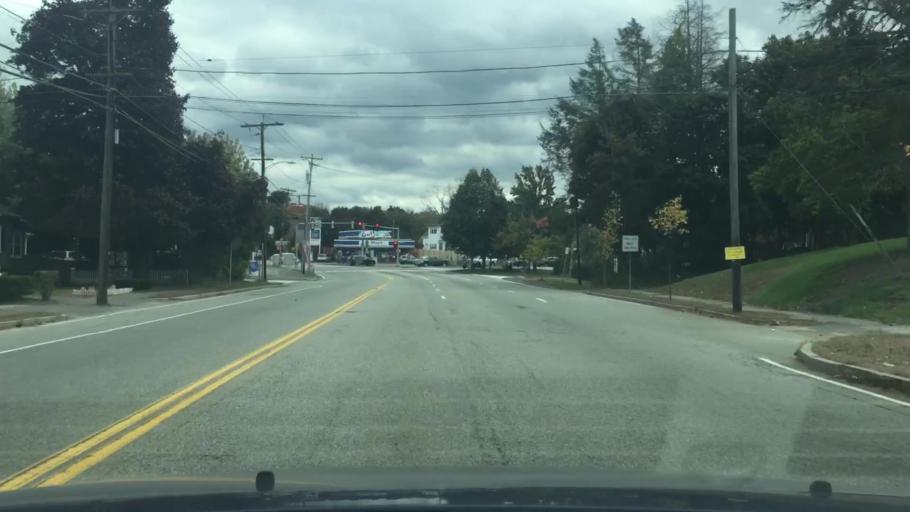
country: US
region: Massachusetts
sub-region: Essex County
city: Haverhill
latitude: 42.7988
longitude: -71.0922
